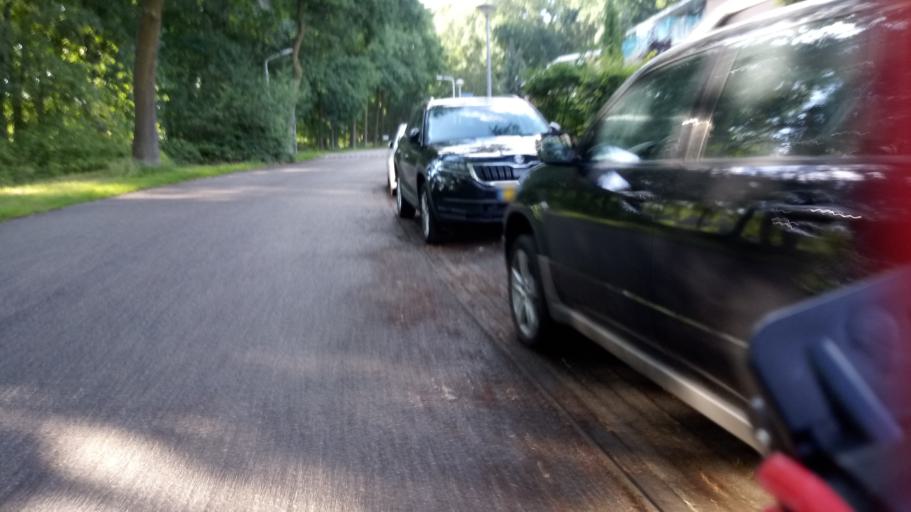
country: NL
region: Gelderland
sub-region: Gemeente Nijmegen
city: Lindenholt
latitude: 51.8106
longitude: 5.8159
